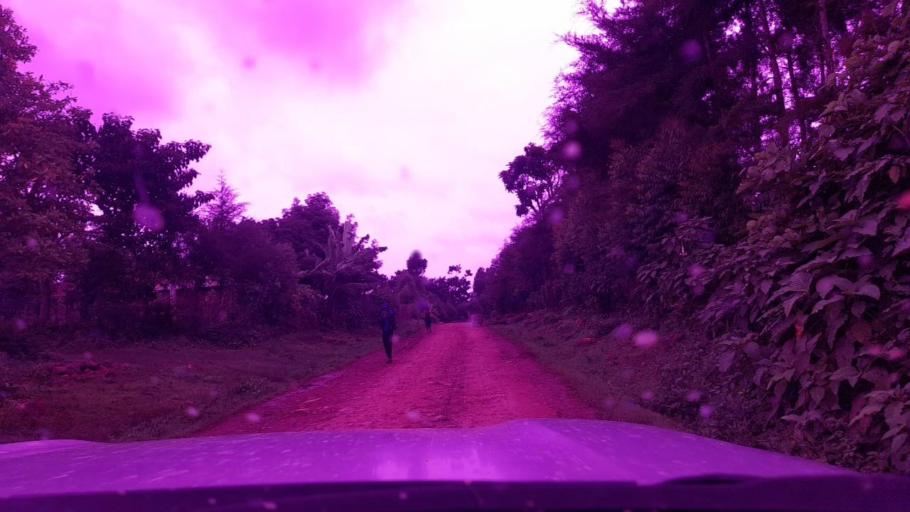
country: ET
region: Southern Nations, Nationalities, and People's Region
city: Bonga
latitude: 7.5499
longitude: 35.8663
